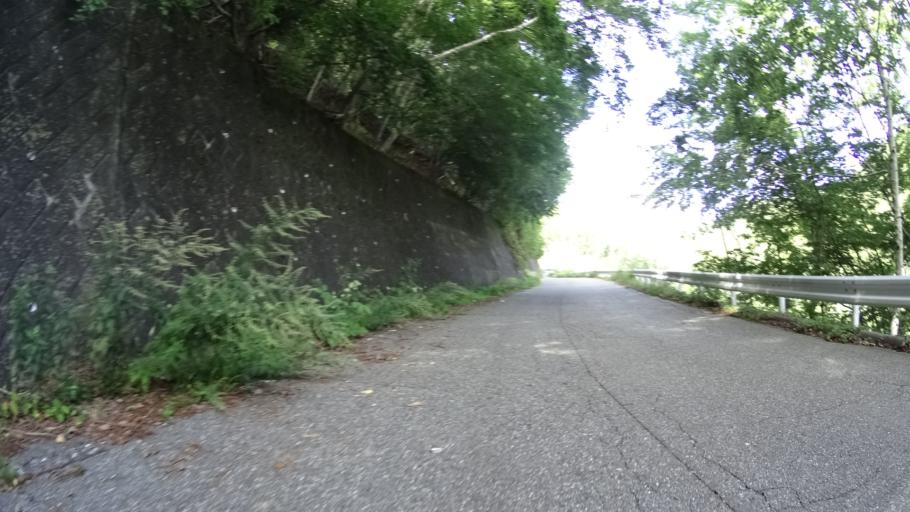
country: JP
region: Yamanashi
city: Nirasaki
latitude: 35.9091
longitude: 138.5411
